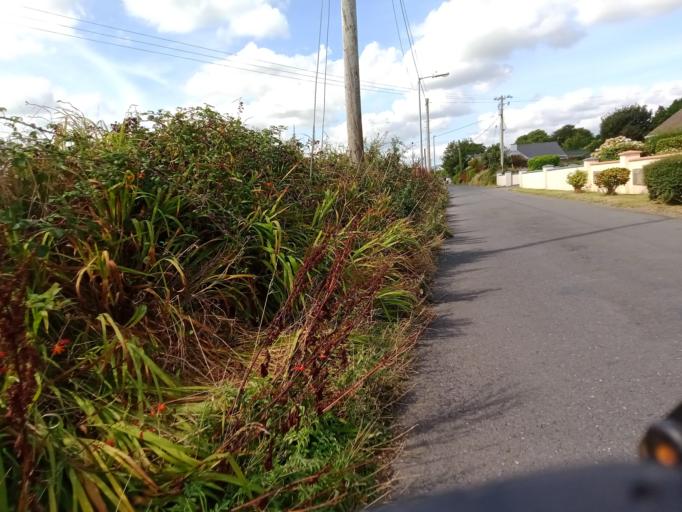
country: IE
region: Munster
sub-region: Waterford
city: Dungarvan
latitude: 52.1294
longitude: -7.4557
